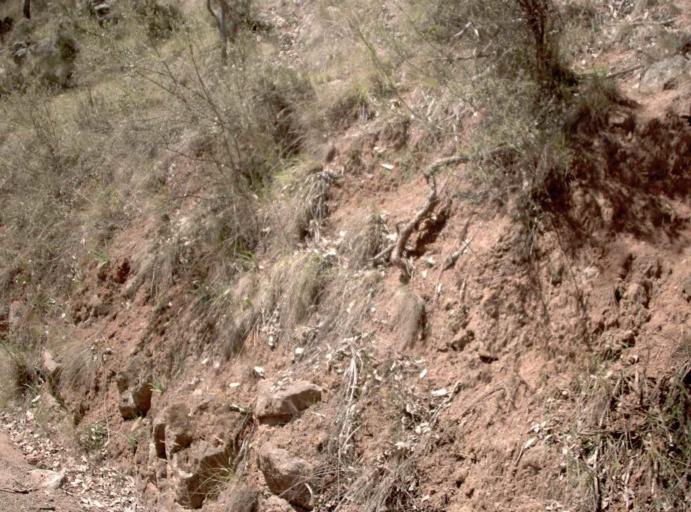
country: AU
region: New South Wales
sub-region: Snowy River
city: Jindabyne
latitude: -37.0651
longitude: 148.5046
